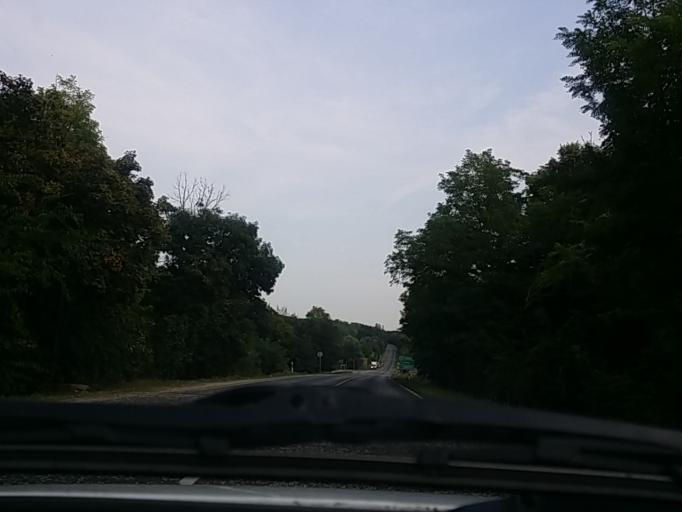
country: HU
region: Fejer
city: Etyek
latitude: 47.4921
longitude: 18.7621
